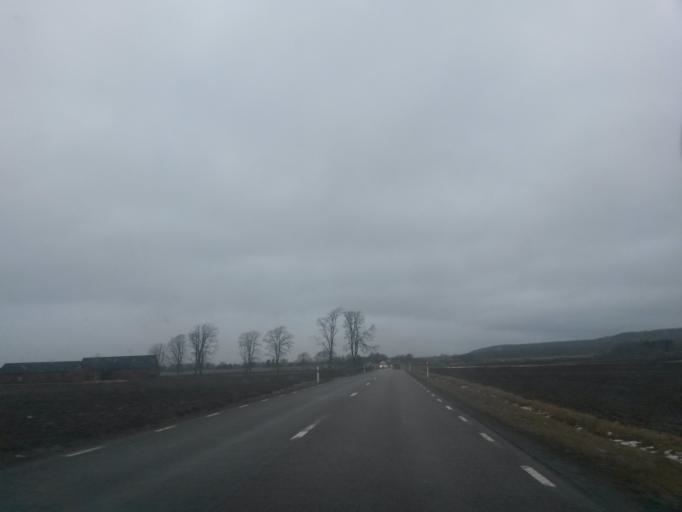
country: SE
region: Vaestra Goetaland
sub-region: Vanersborgs Kommun
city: Vargon
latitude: 58.2808
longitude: 12.3971
